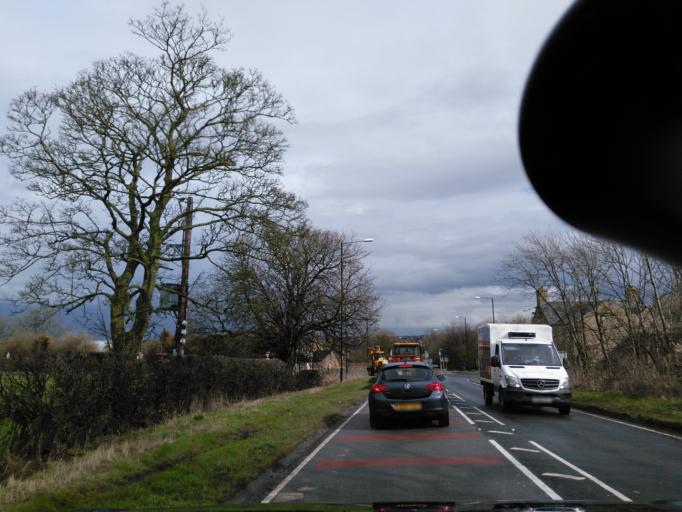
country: GB
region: England
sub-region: North Yorkshire
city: Harrogate
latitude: 54.0079
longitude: -1.5794
